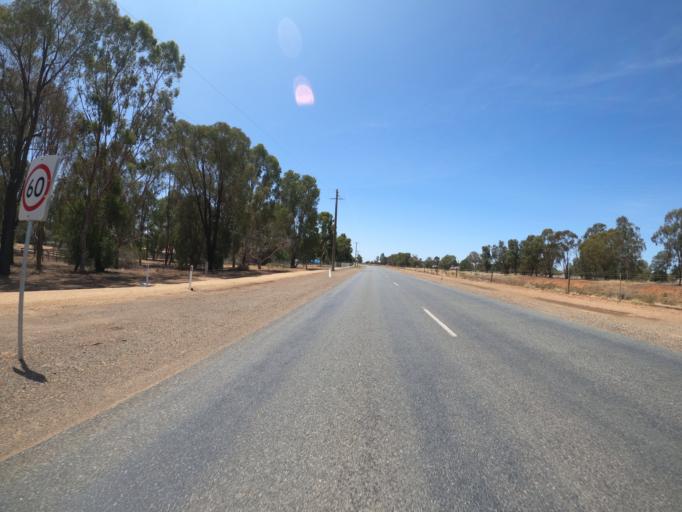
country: AU
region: Victoria
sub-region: Moira
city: Yarrawonga
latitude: -36.0150
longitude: 145.9967
